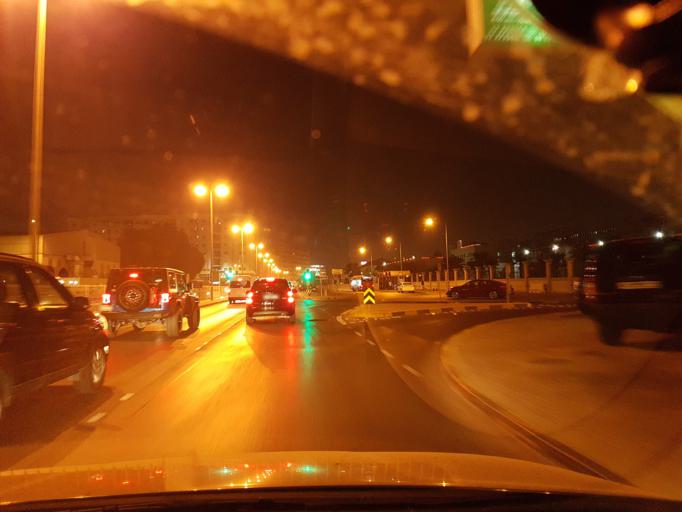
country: BH
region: Manama
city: Manama
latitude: 26.2186
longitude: 50.5692
